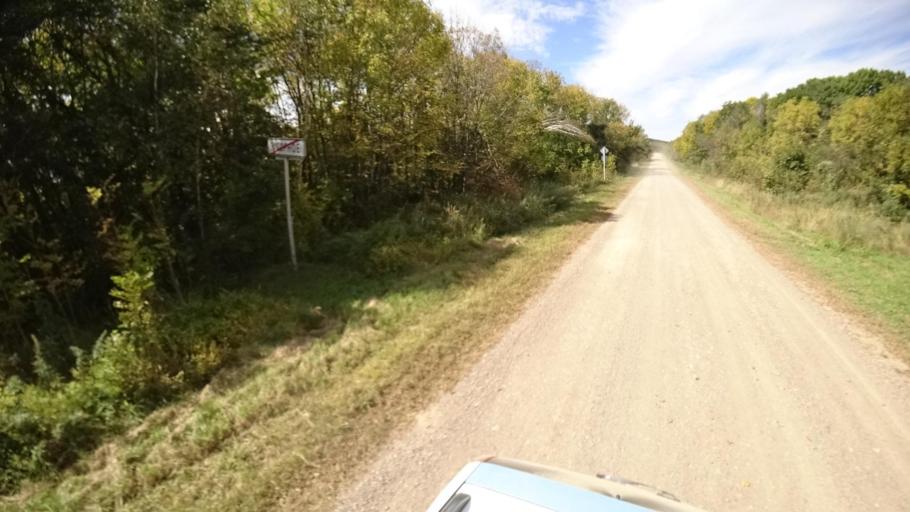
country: RU
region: Primorskiy
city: Yakovlevka
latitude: 44.6582
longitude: 133.7358
